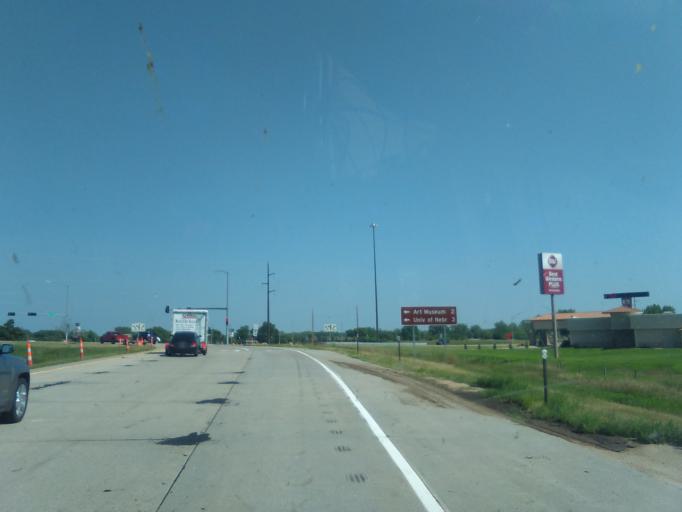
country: US
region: Nebraska
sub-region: Buffalo County
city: Kearney
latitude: 40.6679
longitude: -99.0869
